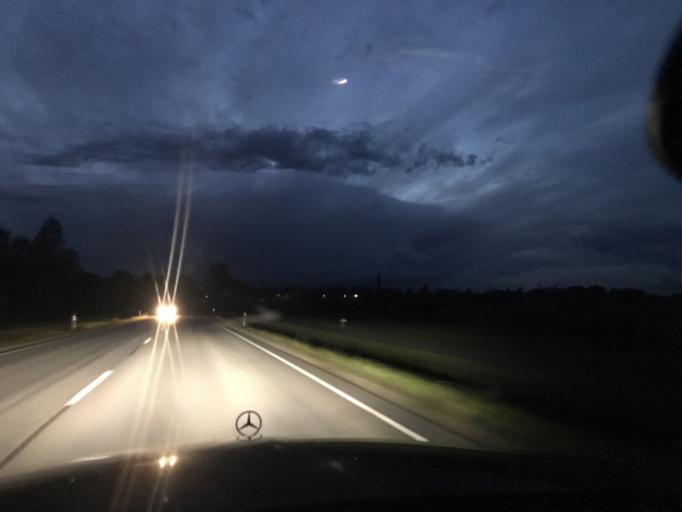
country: EE
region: Valgamaa
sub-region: Torva linn
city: Torva
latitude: 58.0099
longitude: 25.8968
